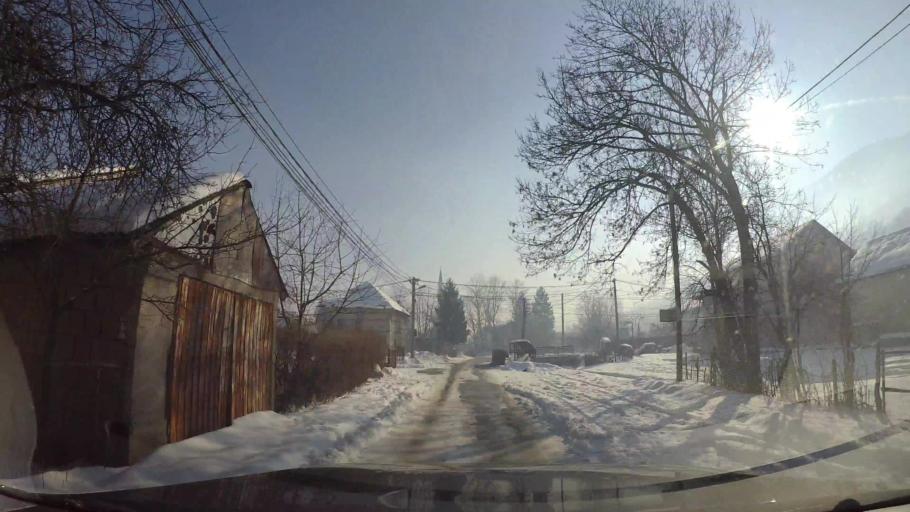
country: BA
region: Federation of Bosnia and Herzegovina
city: Gracanica
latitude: 43.8032
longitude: 18.3002
